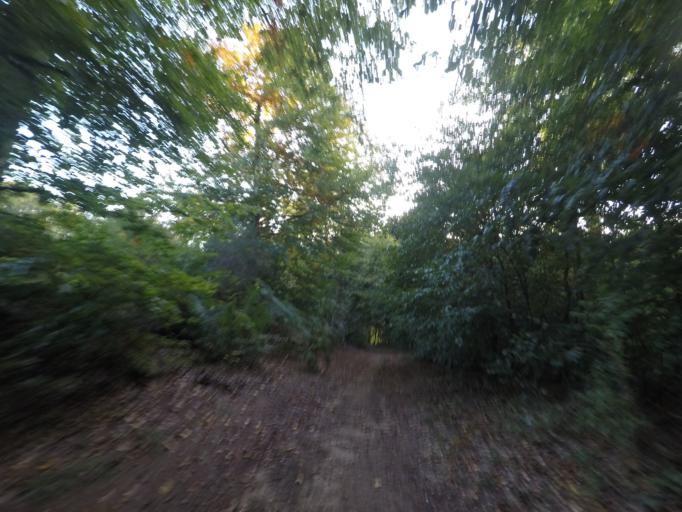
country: LU
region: Luxembourg
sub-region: Canton de Luxembourg
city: Hesperange
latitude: 49.5834
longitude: 6.1523
